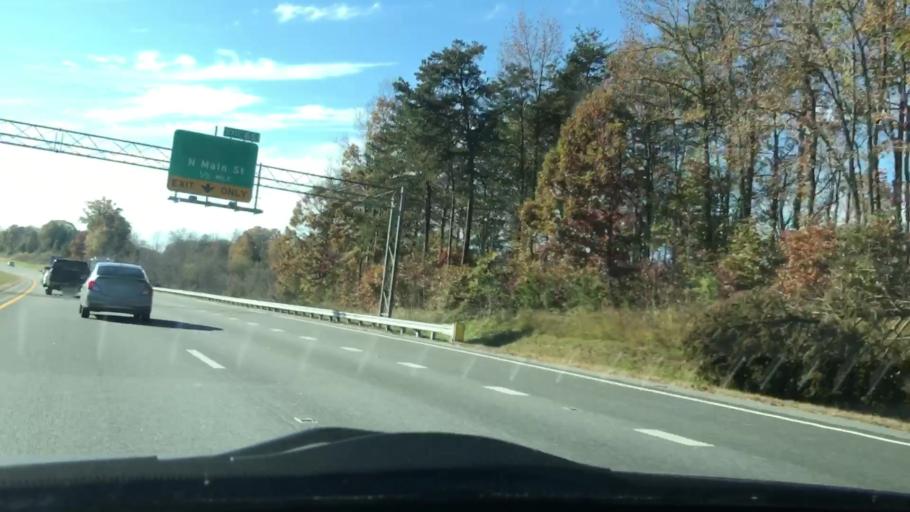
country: US
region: North Carolina
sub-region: Guilford County
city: High Point
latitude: 36.0096
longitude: -80.0151
